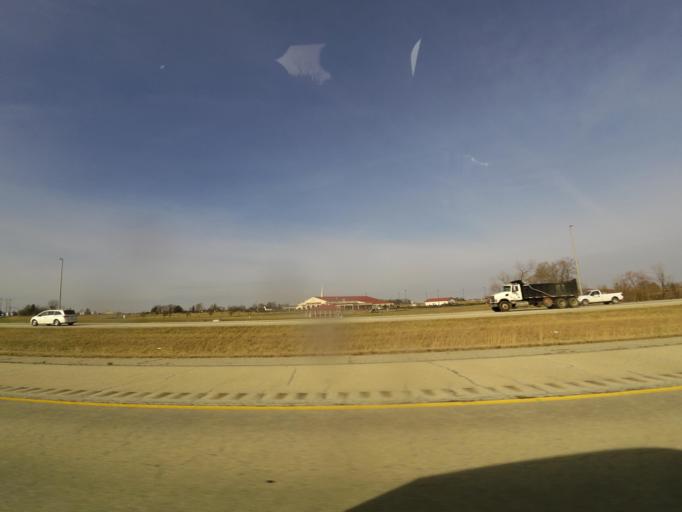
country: US
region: Illinois
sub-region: Macon County
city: Forsyth
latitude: 39.8978
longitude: -89.0019
